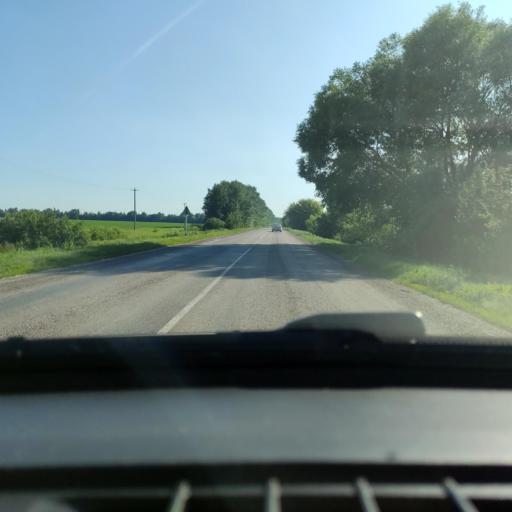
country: RU
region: Voronezj
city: Panino
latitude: 51.5954
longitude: 39.9747
